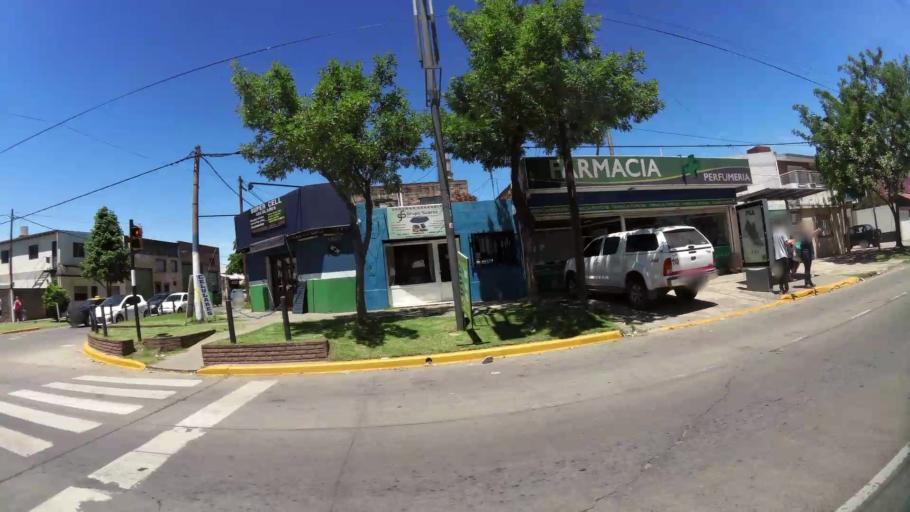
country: AR
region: Santa Fe
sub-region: Departamento de Rosario
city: Rosario
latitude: -32.9482
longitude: -60.6958
